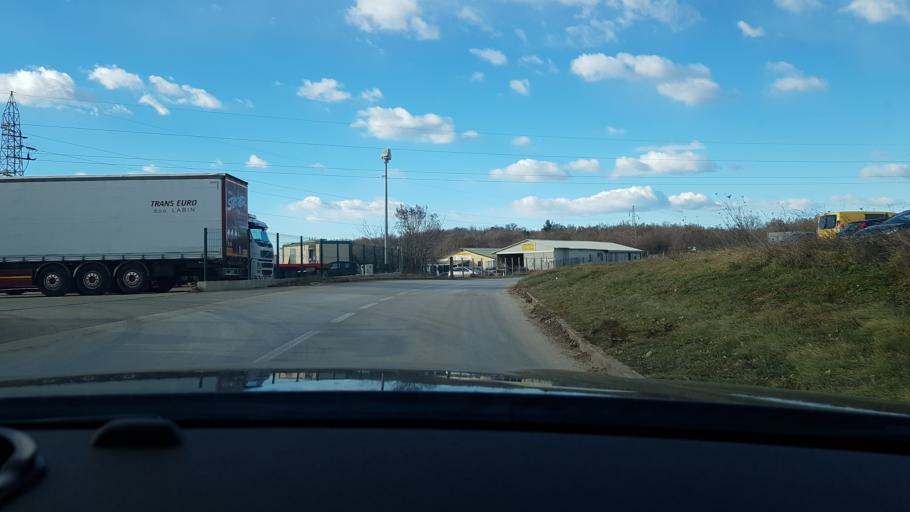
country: HR
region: Istarska
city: Vinez
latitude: 45.1209
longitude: 14.1127
